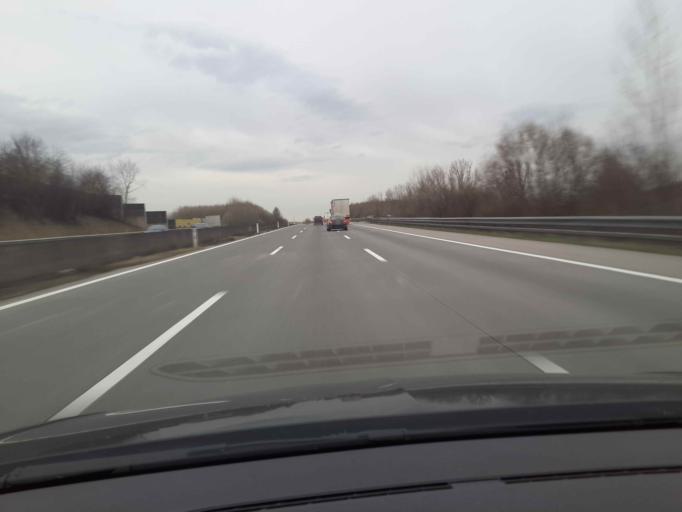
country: AT
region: Lower Austria
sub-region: Politischer Bezirk Amstetten
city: Zeillern
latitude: 48.1195
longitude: 14.7728
